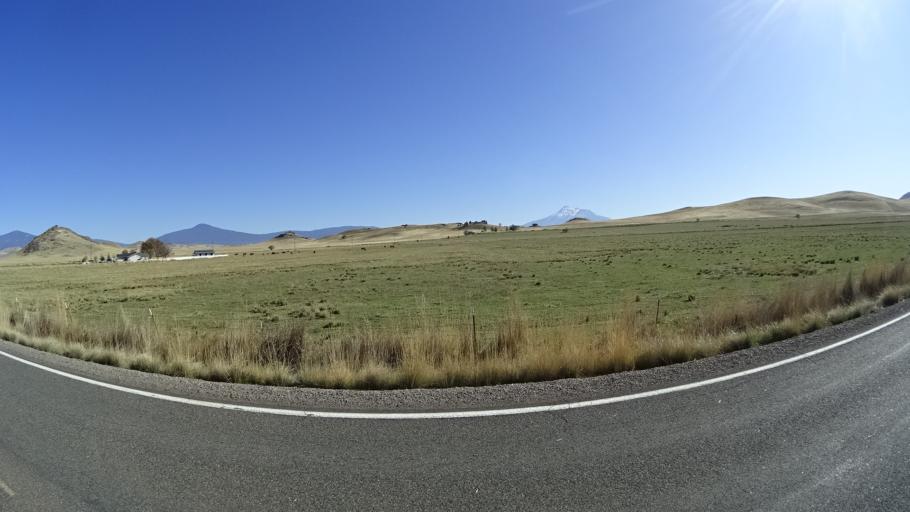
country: US
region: California
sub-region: Siskiyou County
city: Montague
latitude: 41.7483
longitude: -122.5032
